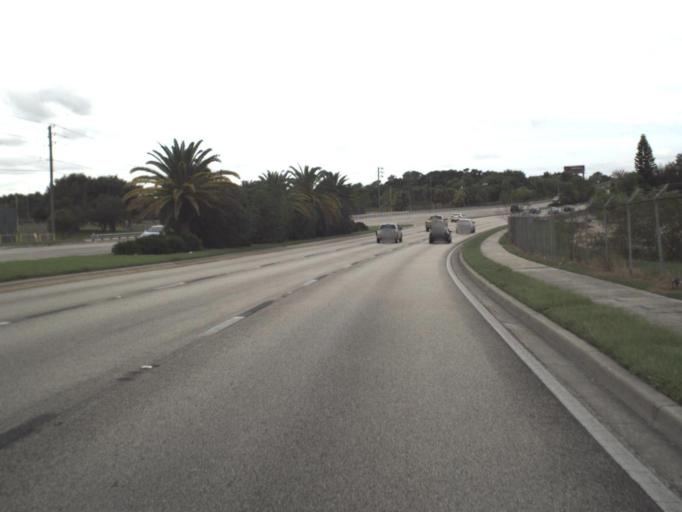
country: US
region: Florida
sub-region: Polk County
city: Winter Haven
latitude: 28.0024
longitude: -81.7315
